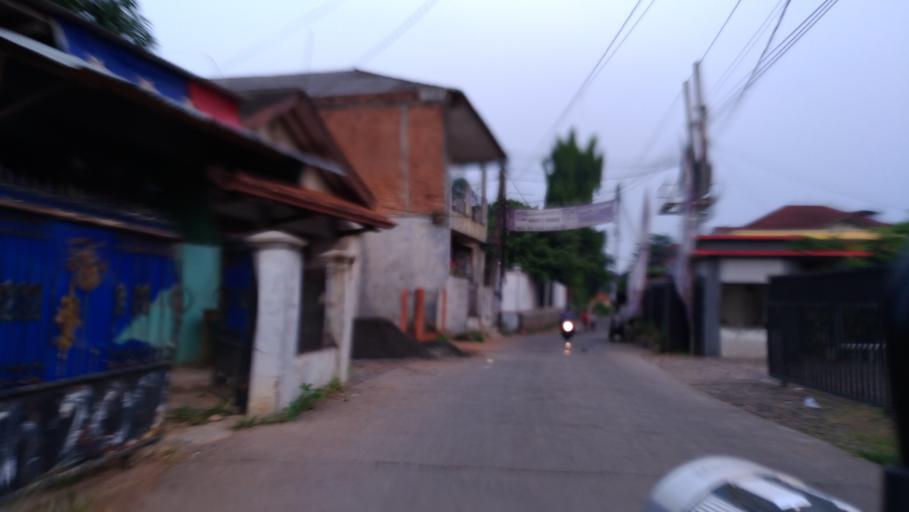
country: ID
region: West Java
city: Depok
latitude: -6.3608
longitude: 106.8663
